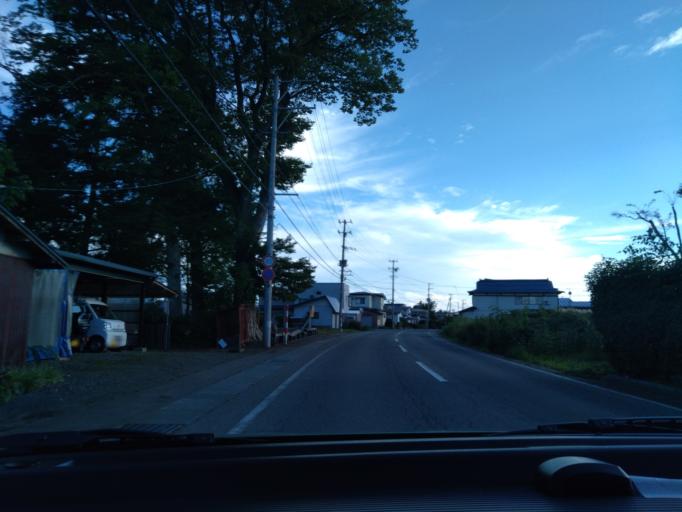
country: JP
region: Akita
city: Omagari
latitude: 39.4181
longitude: 140.4860
